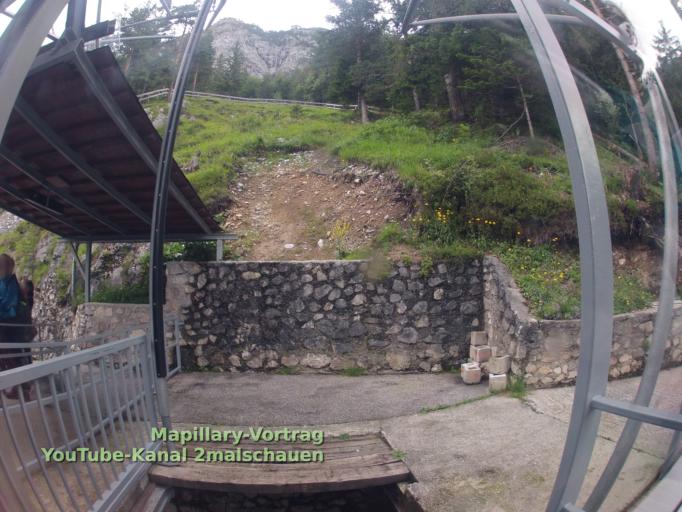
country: AT
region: Salzburg
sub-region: Politischer Bezirk Sankt Johann im Pongau
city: Werfen
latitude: 47.5038
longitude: 13.1903
